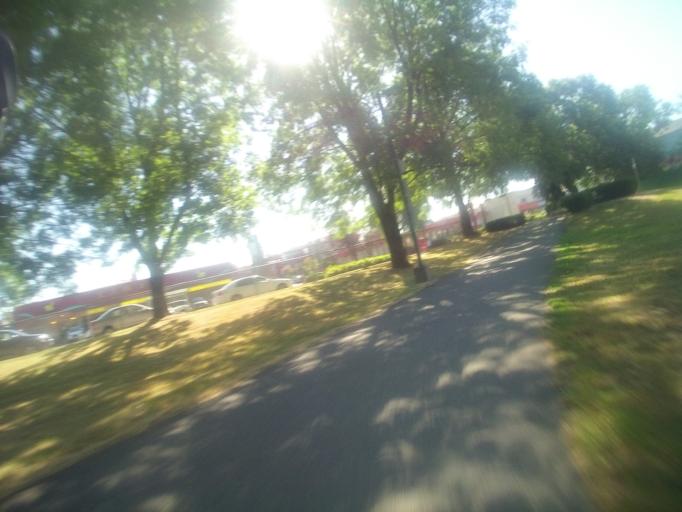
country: CA
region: British Columbia
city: Vancouver
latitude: 49.2362
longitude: -123.0659
